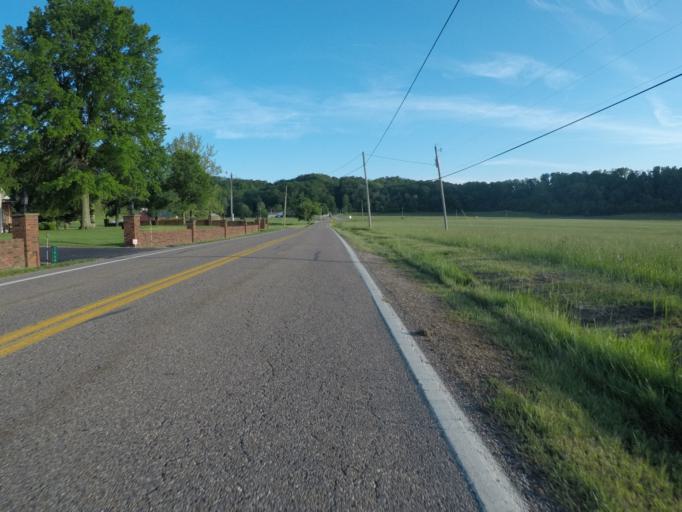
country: US
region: West Virginia
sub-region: Cabell County
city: Huntington
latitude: 38.5262
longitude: -82.4597
